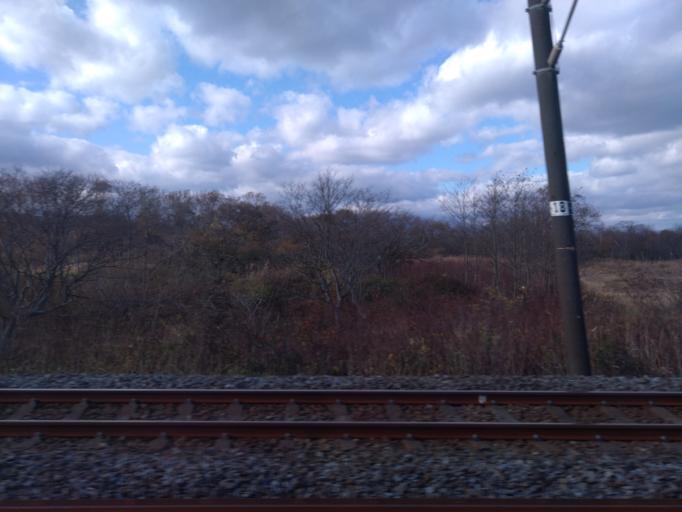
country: JP
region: Hokkaido
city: Shiraoi
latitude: 42.5008
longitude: 141.2730
